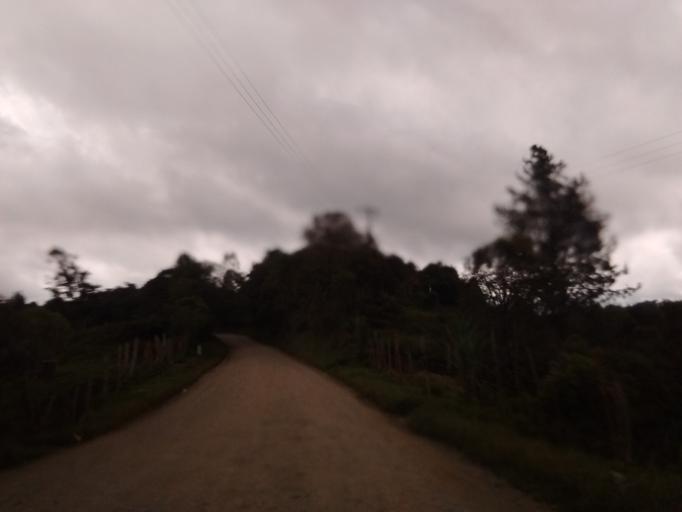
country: CO
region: Huila
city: Isnos
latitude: 2.0319
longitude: -76.2745
